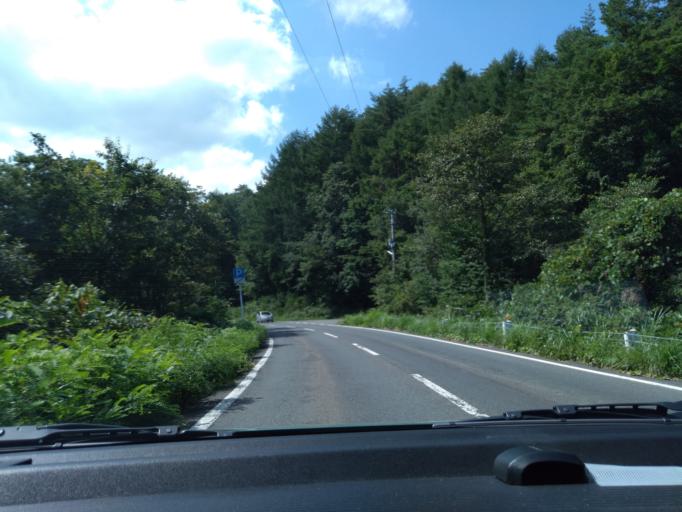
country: JP
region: Iwate
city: Shizukuishi
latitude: 39.6399
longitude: 141.0148
